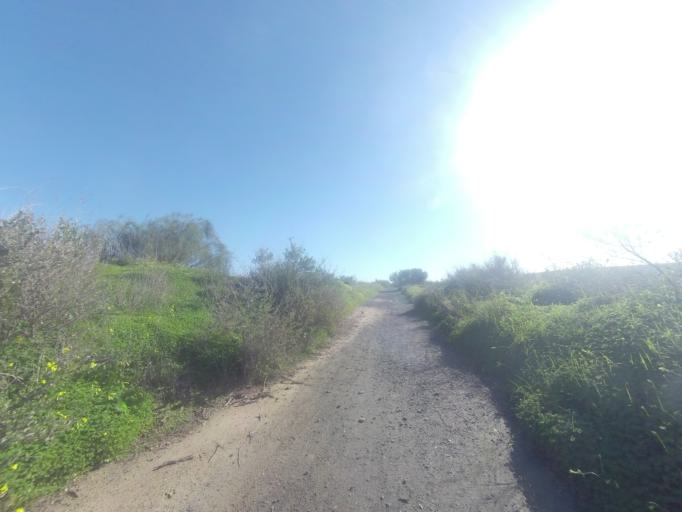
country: ES
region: Andalusia
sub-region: Provincia de Huelva
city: Huelva
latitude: 37.2586
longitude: -6.9179
